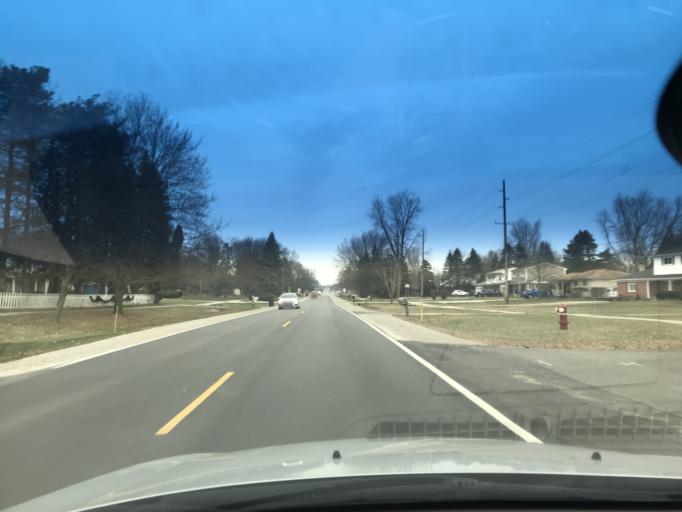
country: US
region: Michigan
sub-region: Macomb County
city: Shelby
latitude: 42.6930
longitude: -83.0543
